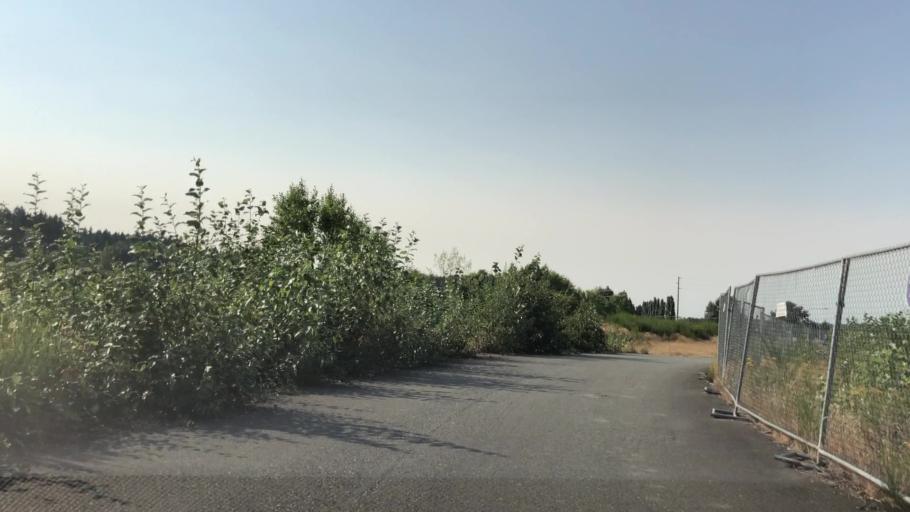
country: US
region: Washington
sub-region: King County
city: Woodinville
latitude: 47.7307
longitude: -122.1430
